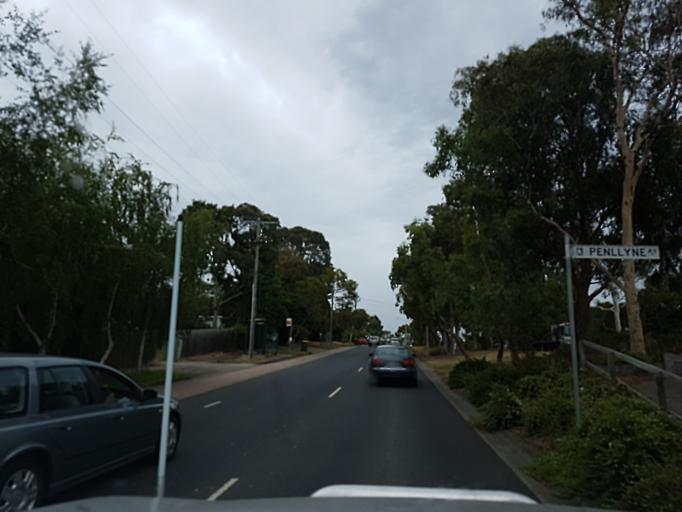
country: AU
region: Victoria
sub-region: Whitehorse
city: Vermont
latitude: -37.8420
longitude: 145.2046
